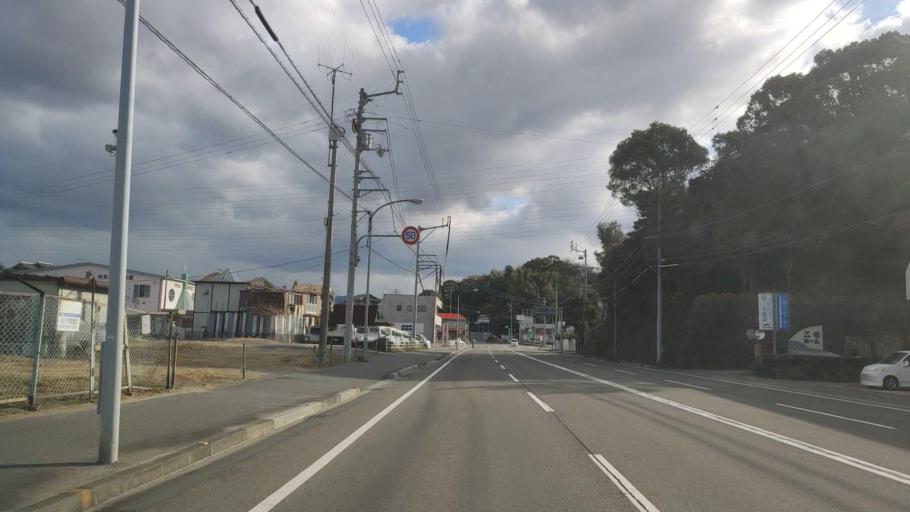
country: JP
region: Ehime
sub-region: Shikoku-chuo Shi
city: Matsuyama
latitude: 33.8563
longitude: 132.7326
